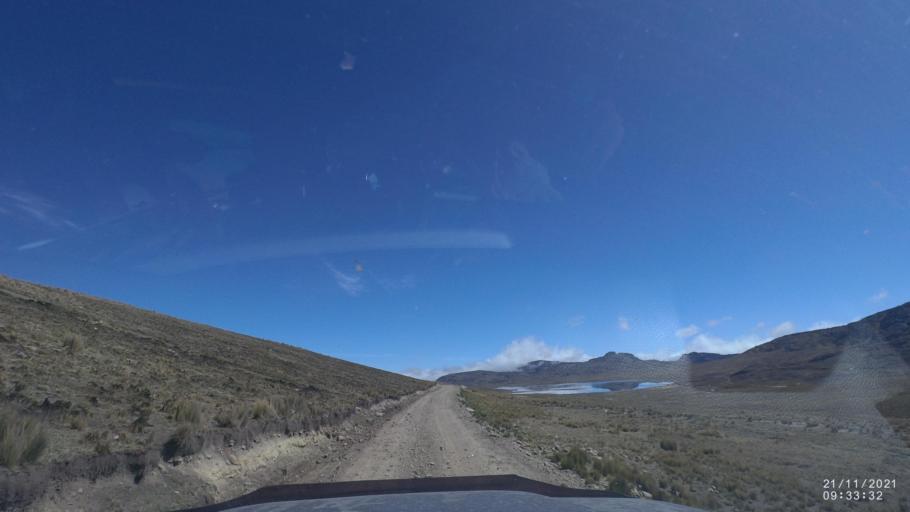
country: BO
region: Cochabamba
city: Cochabamba
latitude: -17.0609
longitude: -66.2582
